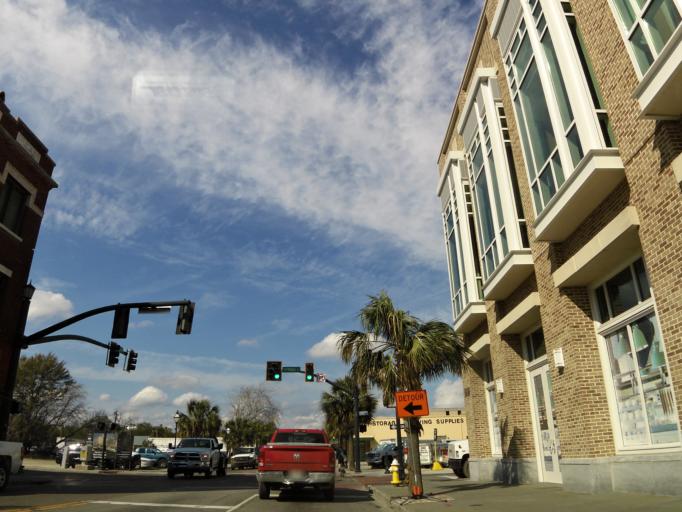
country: US
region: South Carolina
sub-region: Charleston County
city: Charleston
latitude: 32.7929
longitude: -79.9411
